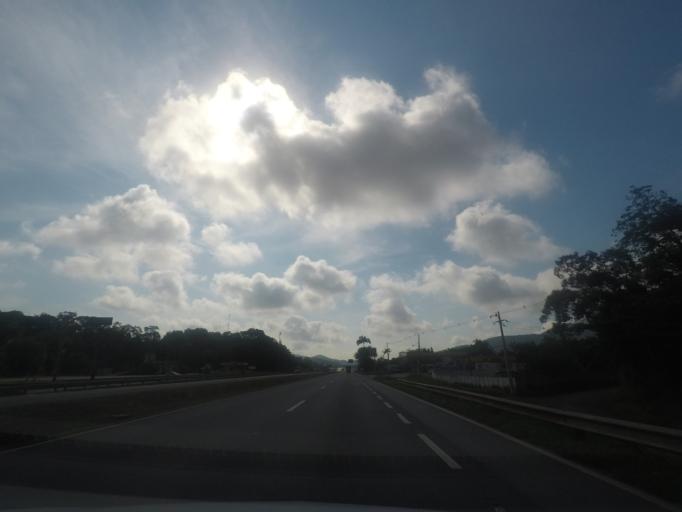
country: BR
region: Parana
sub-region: Antonina
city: Antonina
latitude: -25.5521
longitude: -48.7987
